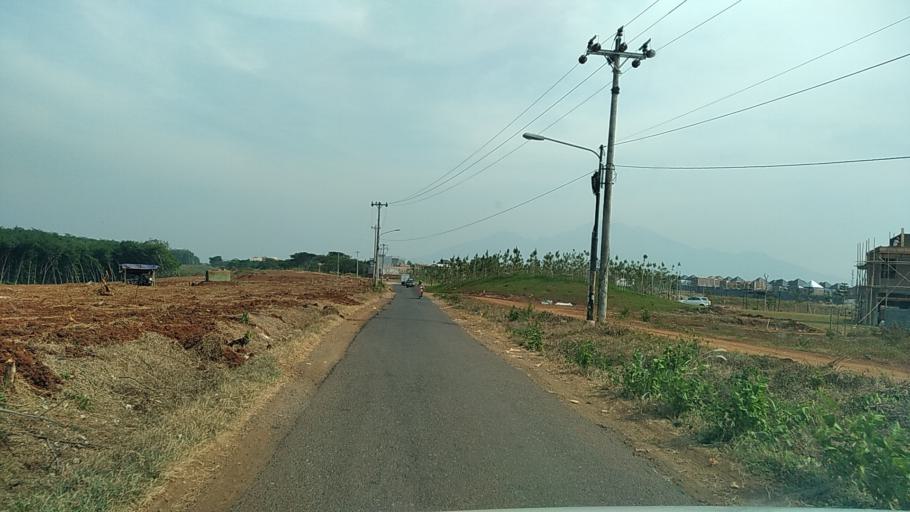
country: ID
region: Central Java
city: Semarang
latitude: -7.0383
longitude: 110.3172
